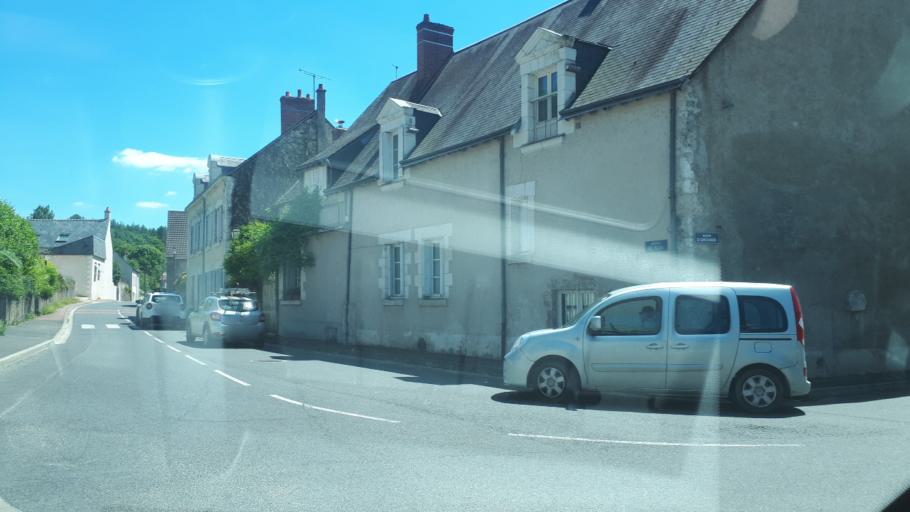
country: FR
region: Centre
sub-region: Departement du Loir-et-Cher
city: Saint-Sulpice-de-Pommeray
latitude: 47.5783
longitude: 1.2159
